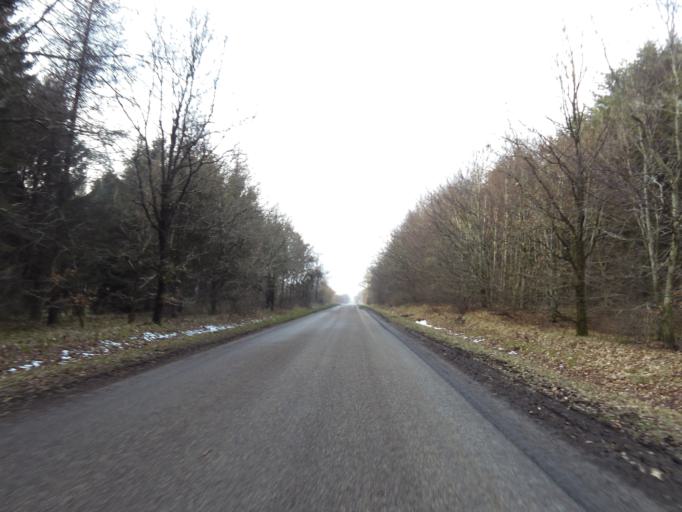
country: DK
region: South Denmark
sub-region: Tonder Kommune
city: Logumkloster
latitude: 55.1631
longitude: 8.8988
